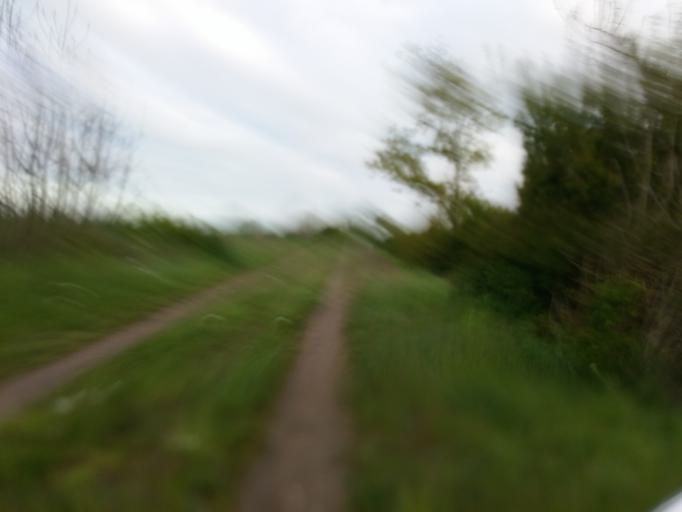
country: DK
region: South Denmark
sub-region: Kerteminde Kommune
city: Munkebo
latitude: 55.4313
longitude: 10.5432
